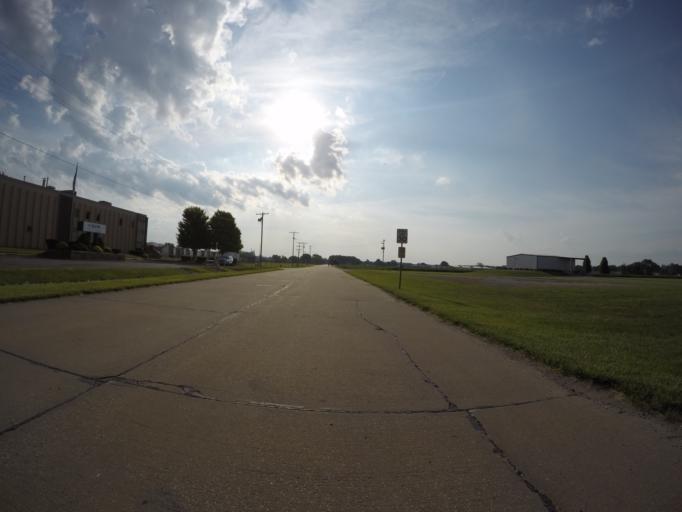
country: US
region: Kansas
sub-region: Doniphan County
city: Elwood
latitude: 39.7517
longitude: -94.8884
